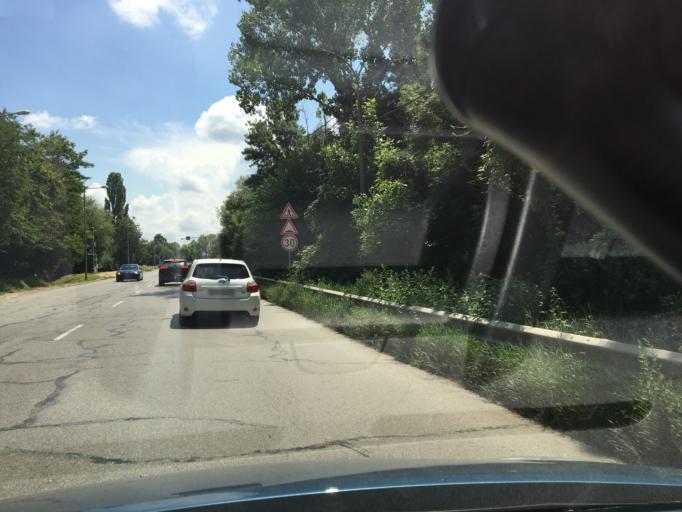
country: BG
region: Sofia-Capital
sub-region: Stolichna Obshtina
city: Sofia
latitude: 42.6610
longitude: 23.3048
